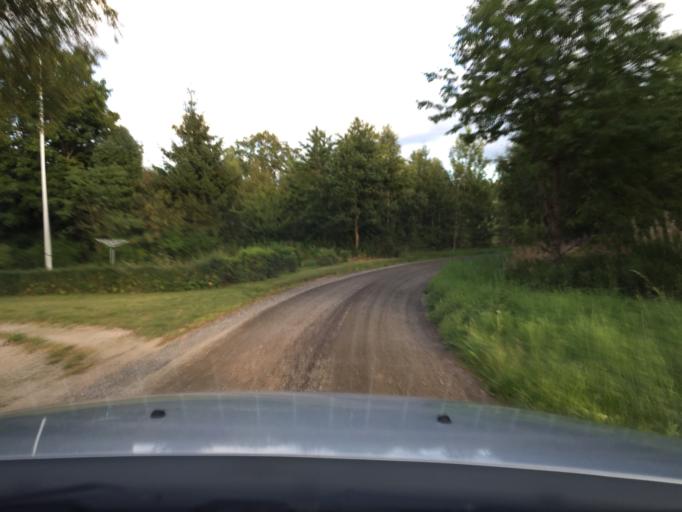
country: SE
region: Skane
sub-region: Hassleholms Kommun
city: Sosdala
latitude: 56.0367
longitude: 13.7119
